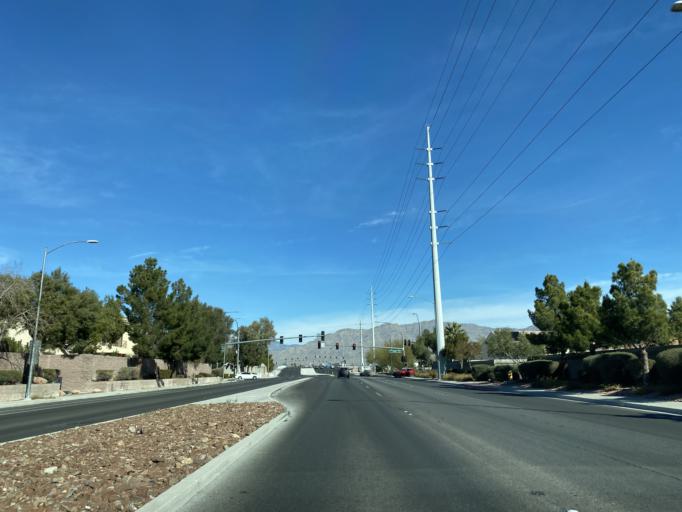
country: US
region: Nevada
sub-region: Clark County
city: North Las Vegas
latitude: 36.2712
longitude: -115.2250
